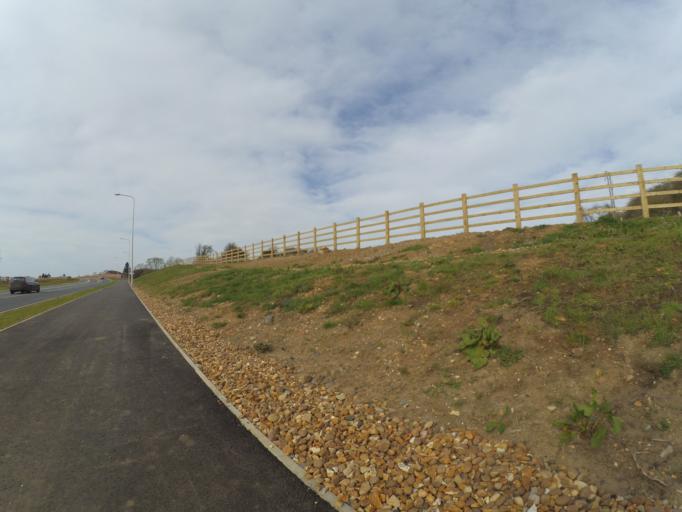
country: GB
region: England
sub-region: Warwickshire
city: Rugby
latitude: 52.3773
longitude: -1.2296
